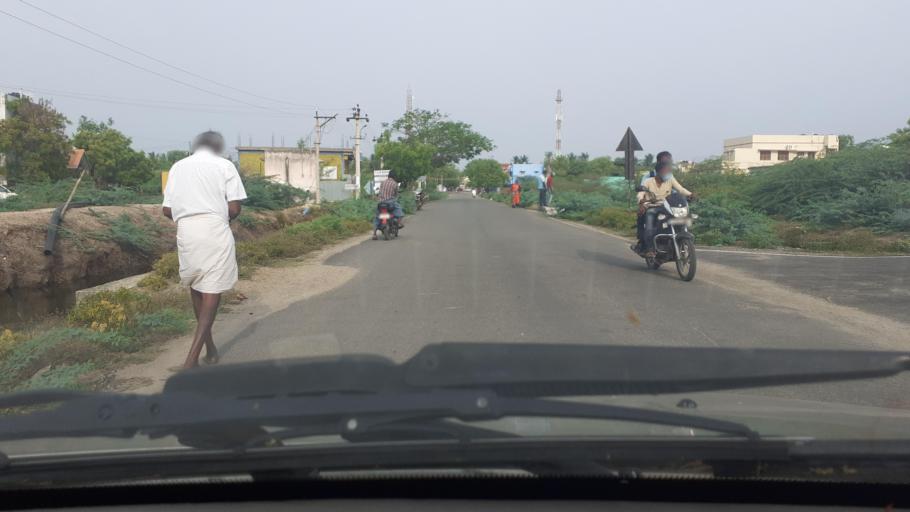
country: IN
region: Tamil Nadu
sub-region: Thoothukkudi
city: Korampallam
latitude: 8.7930
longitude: 78.1092
